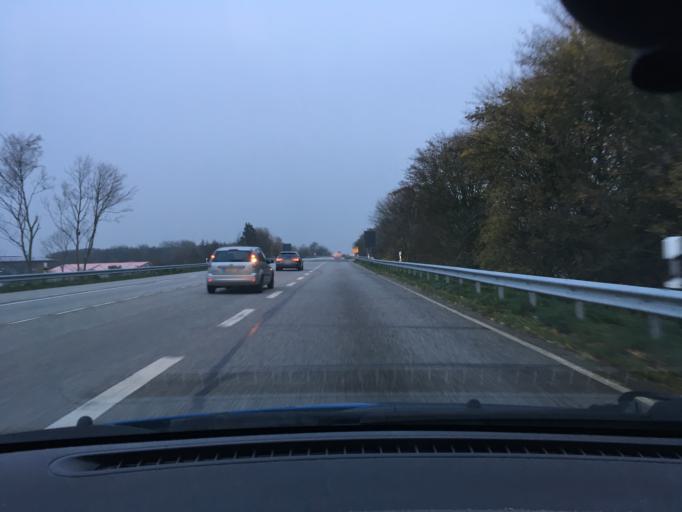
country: DE
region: Schleswig-Holstein
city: Tonning
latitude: 54.3246
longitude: 8.9486
